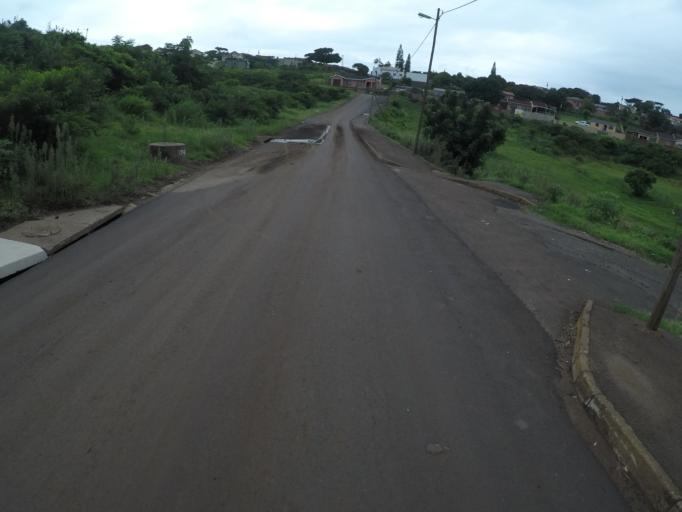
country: ZA
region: KwaZulu-Natal
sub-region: uThungulu District Municipality
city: Empangeni
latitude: -28.7703
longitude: 31.8602
